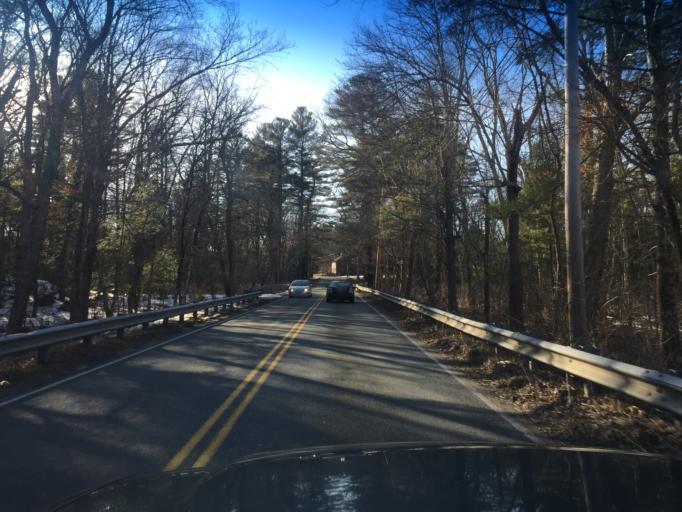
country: US
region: Massachusetts
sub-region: Worcester County
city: Mendon
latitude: 42.0932
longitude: -71.5184
